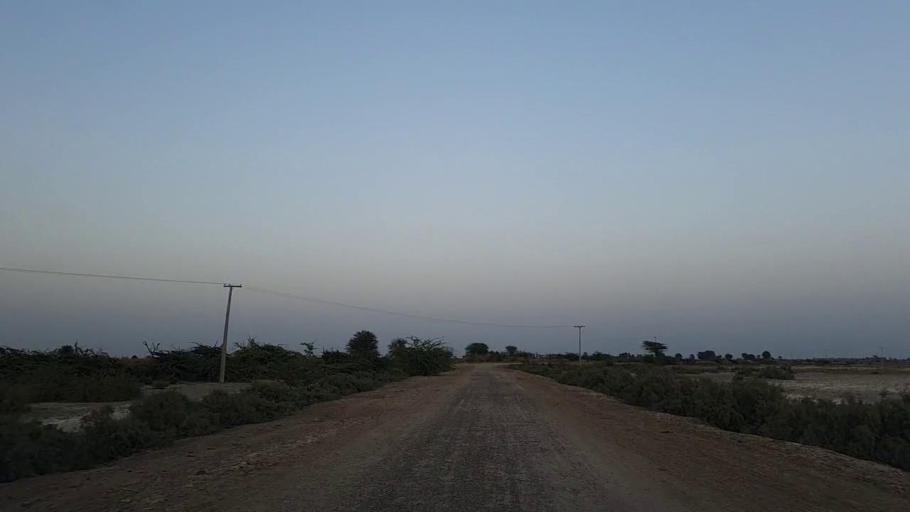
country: PK
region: Sindh
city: Pithoro
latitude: 25.4151
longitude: 69.3095
